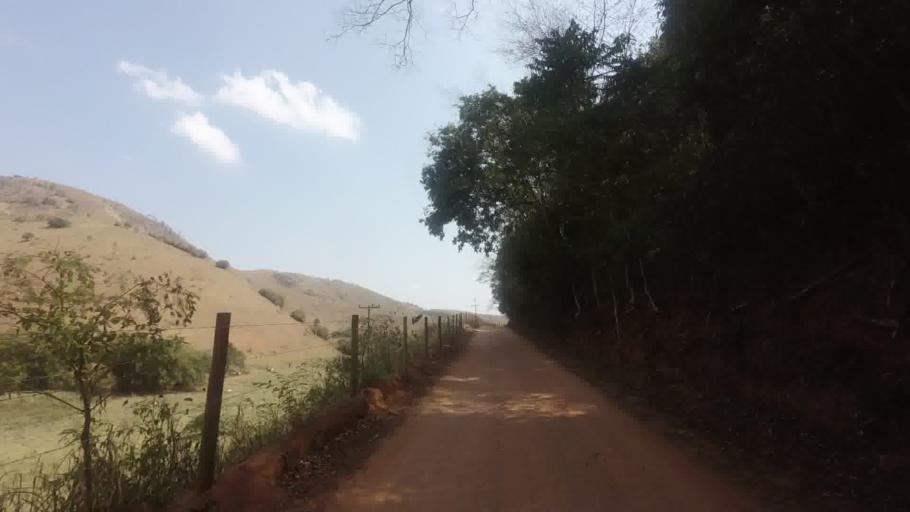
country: BR
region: Espirito Santo
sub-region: Sao Jose Do Calcado
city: Sao Jose do Calcado
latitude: -21.0544
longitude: -41.5310
